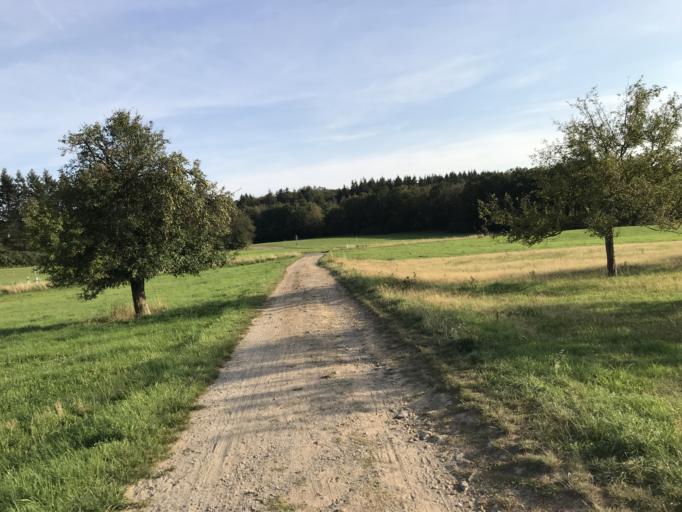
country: DE
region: Hesse
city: Lollar
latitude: 50.6363
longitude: 8.6552
